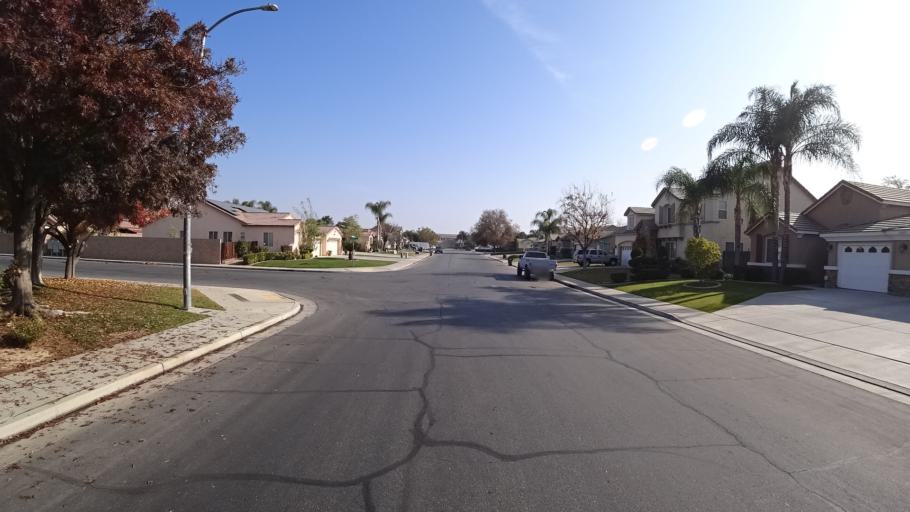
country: US
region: California
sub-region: Kern County
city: Greenacres
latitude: 35.4130
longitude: -119.1242
